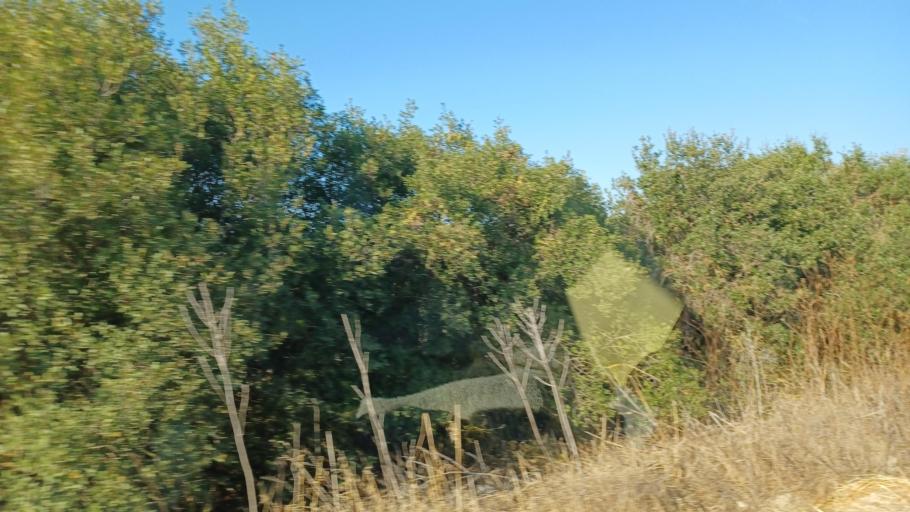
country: CY
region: Pafos
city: Mesogi
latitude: 34.8809
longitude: 32.5159
